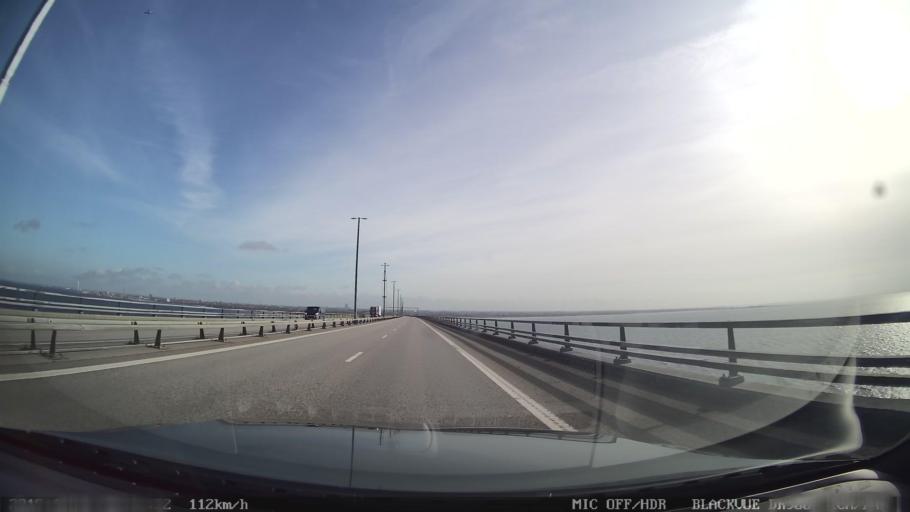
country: SE
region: Skane
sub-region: Malmo
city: Bunkeflostrand
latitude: 55.5696
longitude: 12.8536
